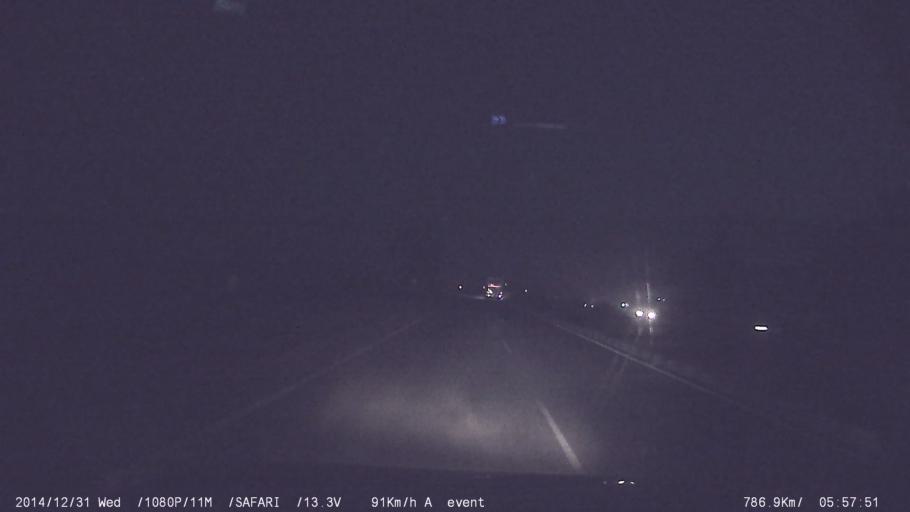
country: IN
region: Tamil Nadu
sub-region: Cuddalore
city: Panruti
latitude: 11.7965
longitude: 79.4080
